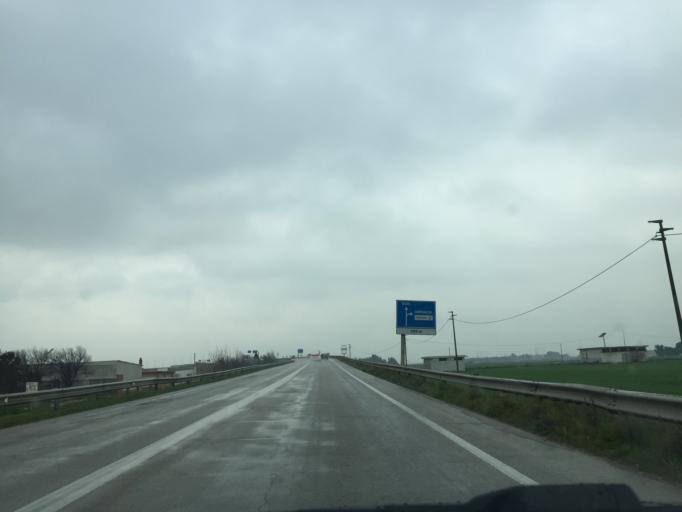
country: IT
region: Apulia
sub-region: Provincia di Foggia
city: Foggia
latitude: 41.4781
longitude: 15.5126
